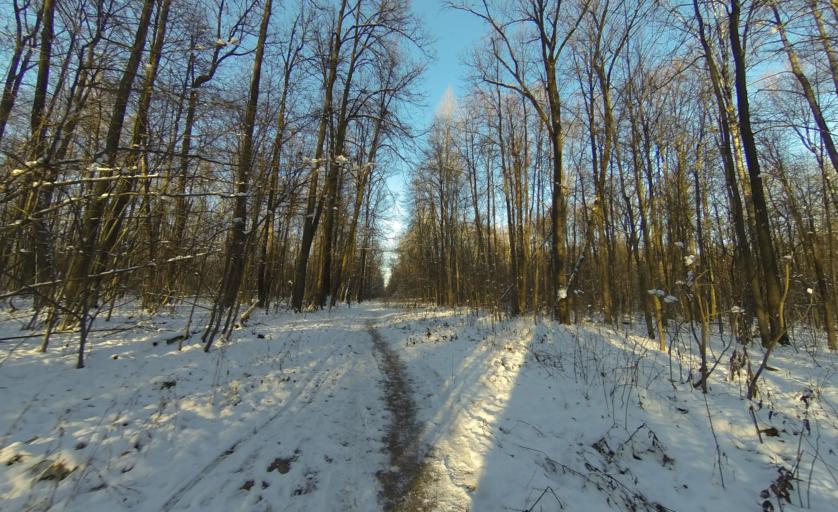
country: RU
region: Moscow
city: Babushkin
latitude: 55.8476
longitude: 37.7618
